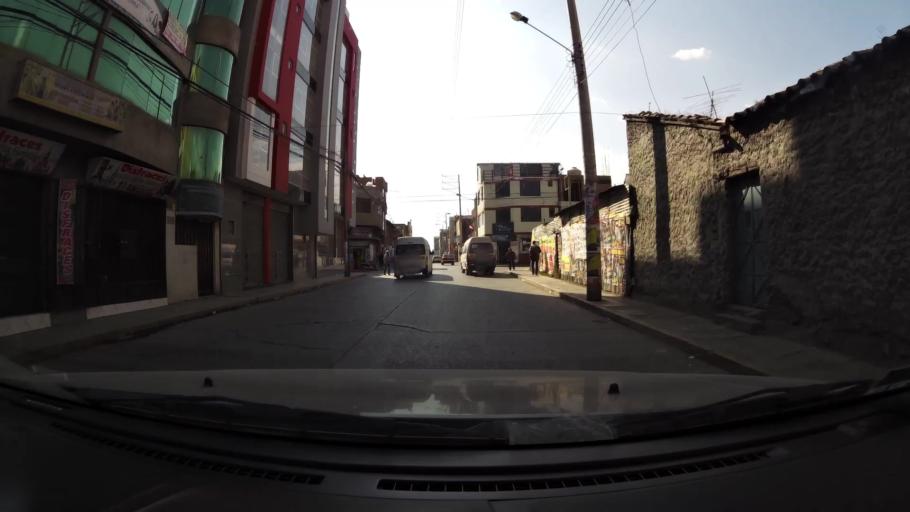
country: PE
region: Junin
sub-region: Provincia de Huancayo
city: El Tambo
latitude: -12.0599
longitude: -75.2131
